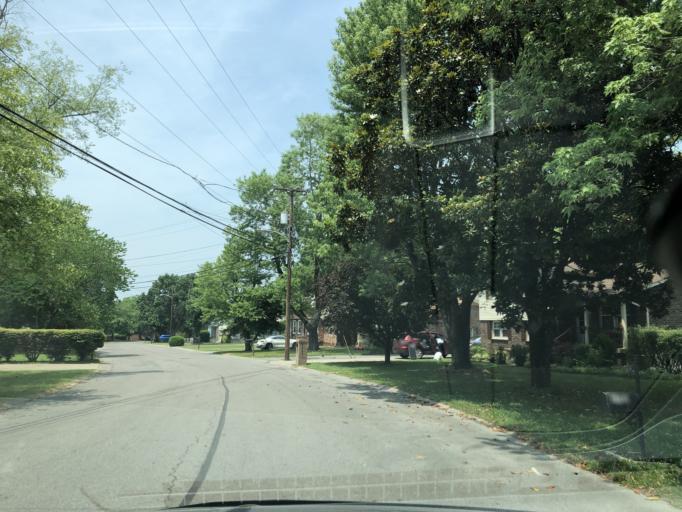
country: US
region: Tennessee
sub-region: Rutherford County
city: La Vergne
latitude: 36.0742
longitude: -86.6722
